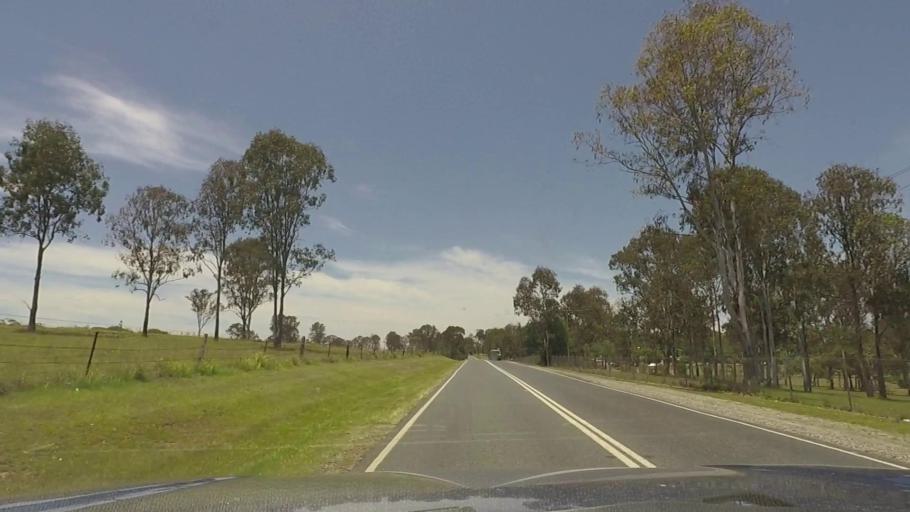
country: AU
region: Queensland
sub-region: Logan
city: North Maclean
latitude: -27.8232
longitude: 153.0270
